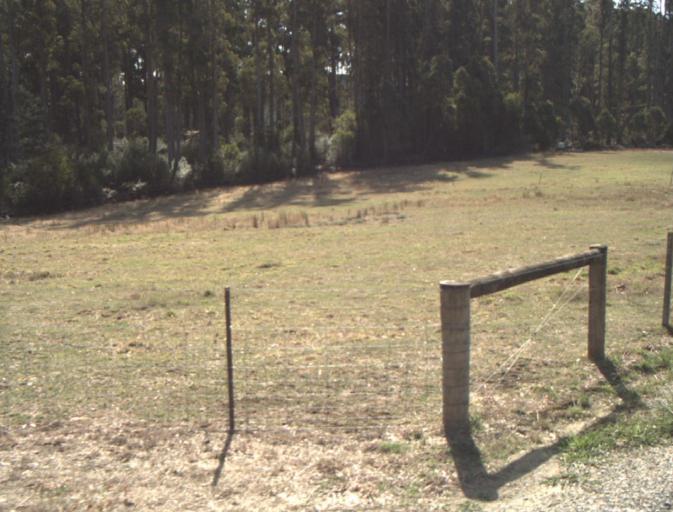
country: AU
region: Tasmania
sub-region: Launceston
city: Mayfield
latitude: -41.2329
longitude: 147.2350
